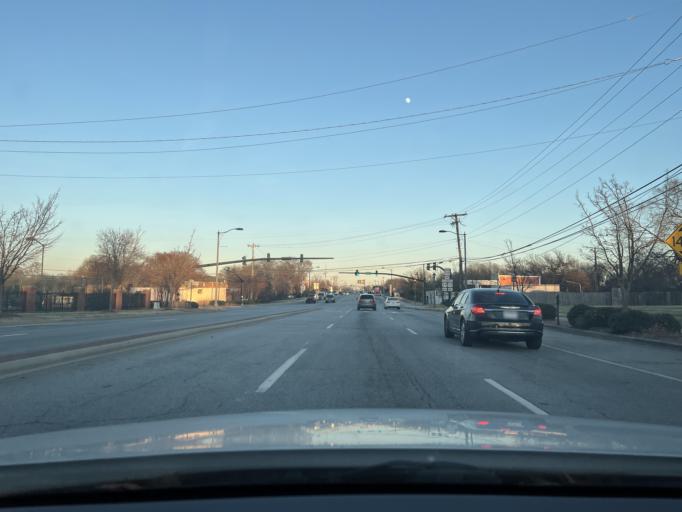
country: US
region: North Carolina
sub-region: Guilford County
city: Greensboro
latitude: 36.0732
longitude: -79.7686
